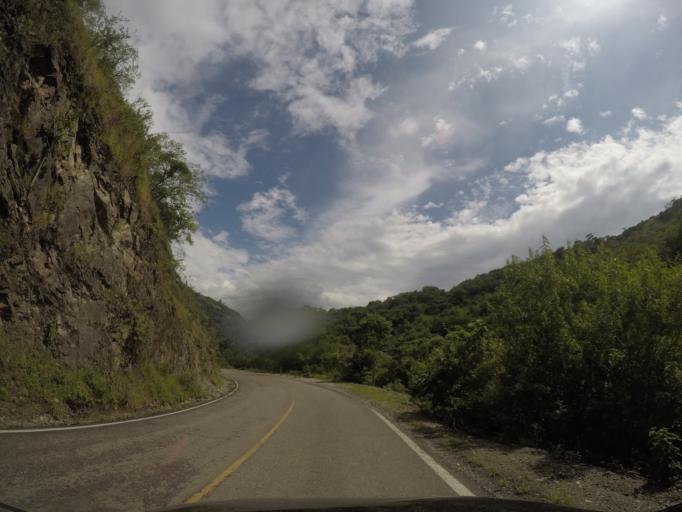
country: MX
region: Oaxaca
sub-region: San Jeronimo Coatlan
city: San Cristobal Honduras
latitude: 16.3698
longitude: -97.0894
